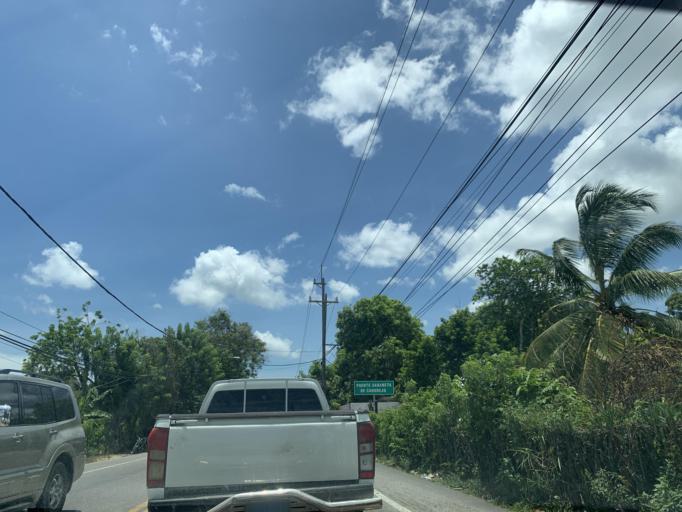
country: DO
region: Puerto Plata
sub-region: Puerto Plata
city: Puerto Plata
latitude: 19.7481
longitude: -70.5930
